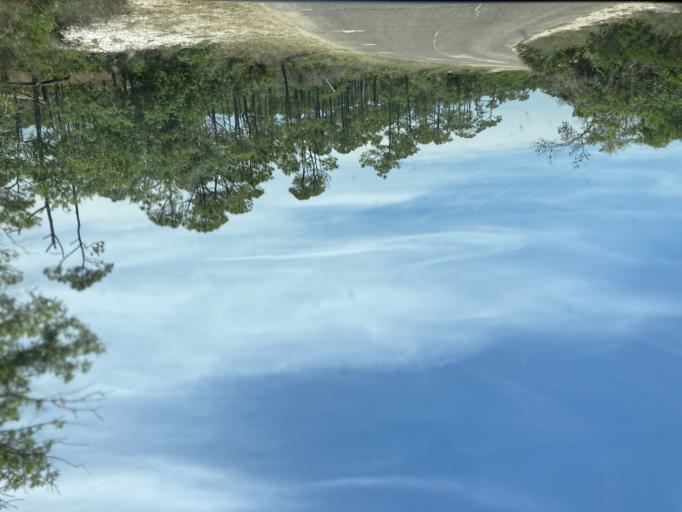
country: US
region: Florida
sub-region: Bay County
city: Lower Grand Lagoon
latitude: 30.1313
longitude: -85.7394
